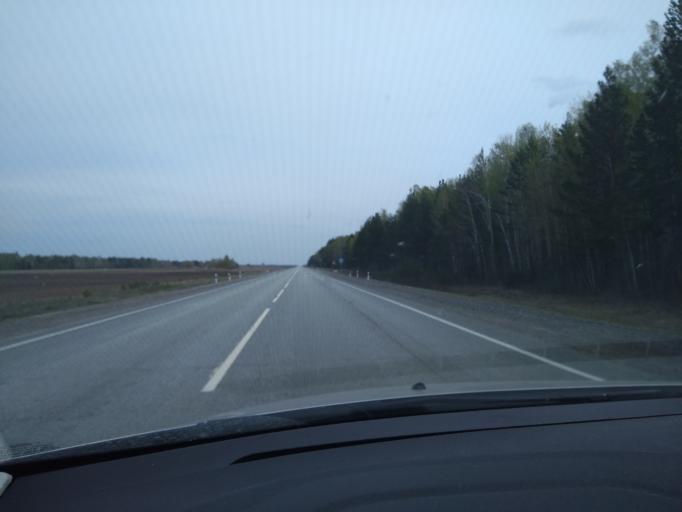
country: RU
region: Sverdlovsk
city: Troitskiy
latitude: 57.0943
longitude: 63.9989
